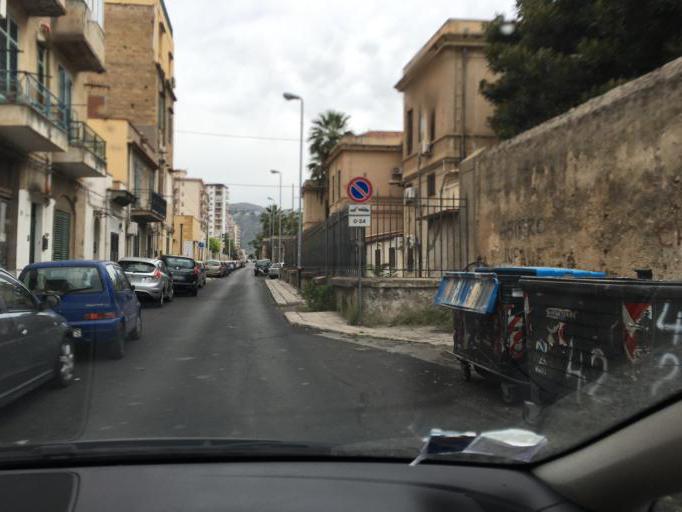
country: IT
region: Sicily
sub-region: Palermo
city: Palermo
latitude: 38.1082
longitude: 13.3375
